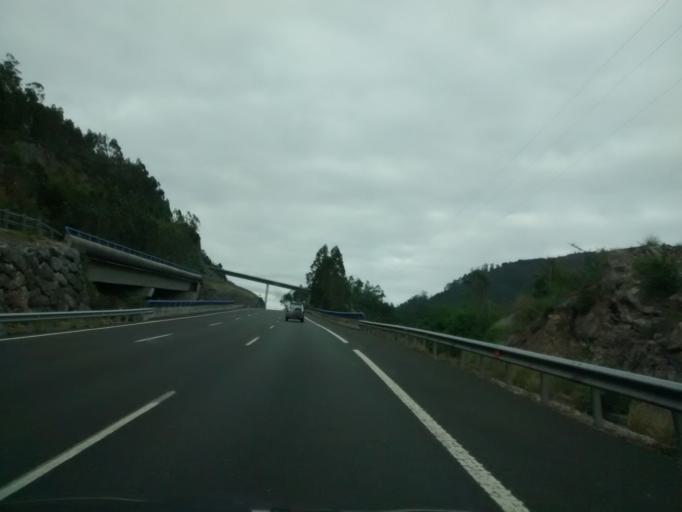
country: ES
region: Cantabria
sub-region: Provincia de Cantabria
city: Los Corrales de Buelna
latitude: 43.2912
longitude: -4.0786
